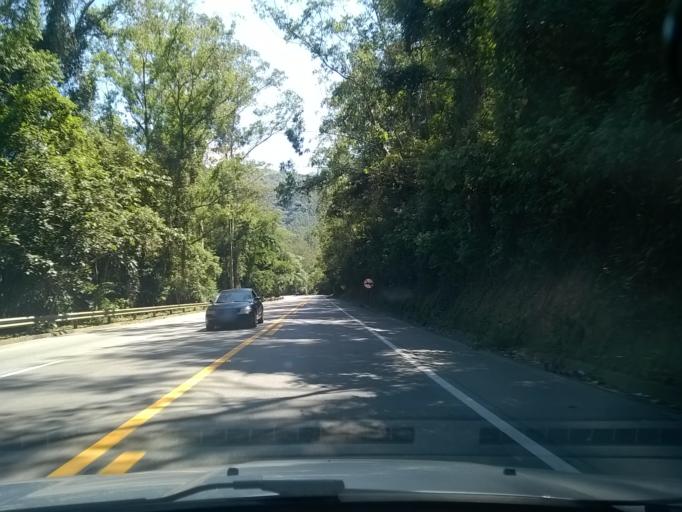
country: BR
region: Sao Paulo
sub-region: Varzea Paulista
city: Varzea Paulista
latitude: -23.2684
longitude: -46.8135
